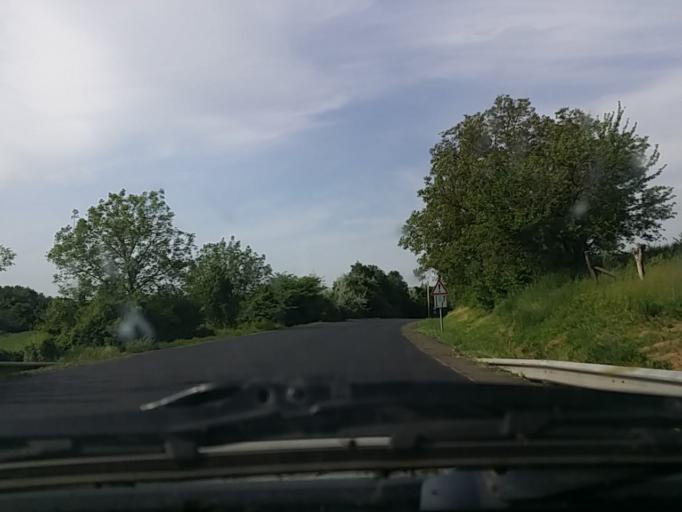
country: HU
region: Baranya
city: Harkany
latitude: 45.9017
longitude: 18.2302
